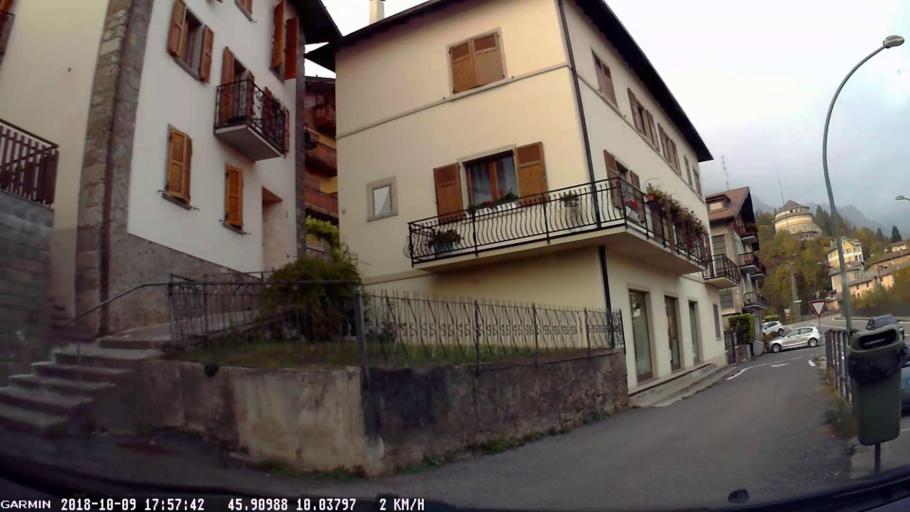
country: IT
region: Lombardy
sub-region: Provincia di Bergamo
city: Castione della Presolana
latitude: 45.9125
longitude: 10.0427
